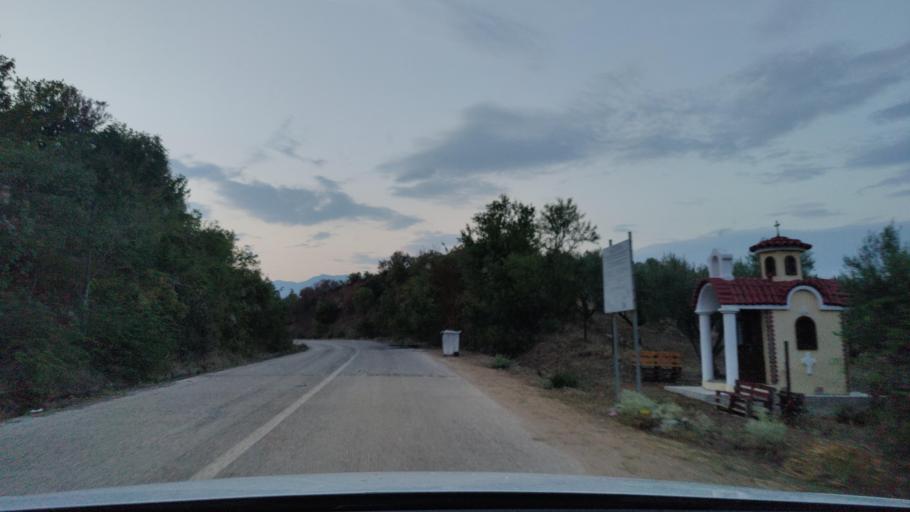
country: GR
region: Central Macedonia
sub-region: Nomos Serron
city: Chrysochorafa
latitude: 41.1484
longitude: 23.2079
